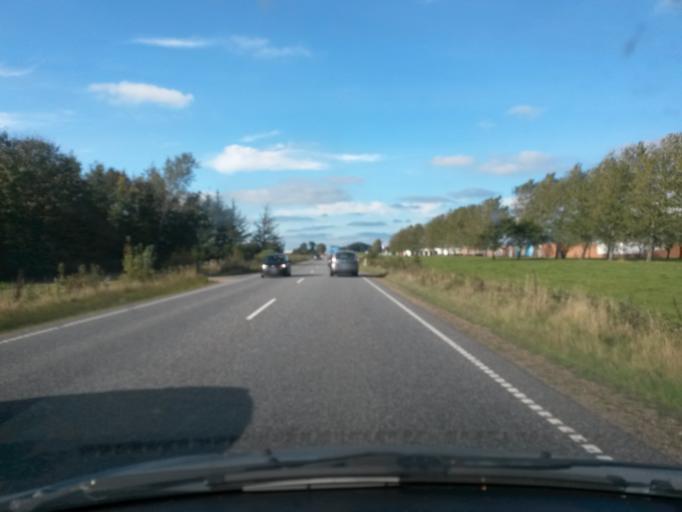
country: DK
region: Central Jutland
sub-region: Herning Kommune
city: Avlum
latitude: 56.2596
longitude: 8.7819
